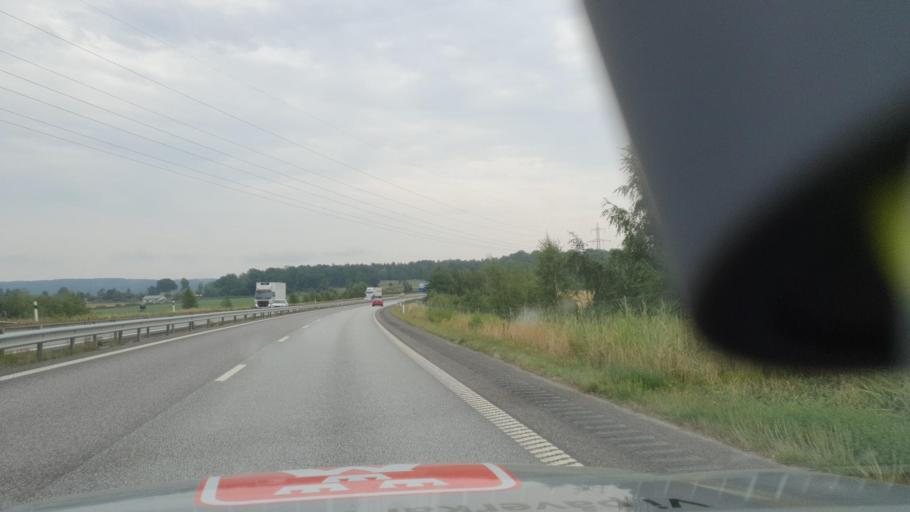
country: SE
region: Blekinge
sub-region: Solvesborgs Kommun
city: Soelvesborg
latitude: 56.0707
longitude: 14.5274
